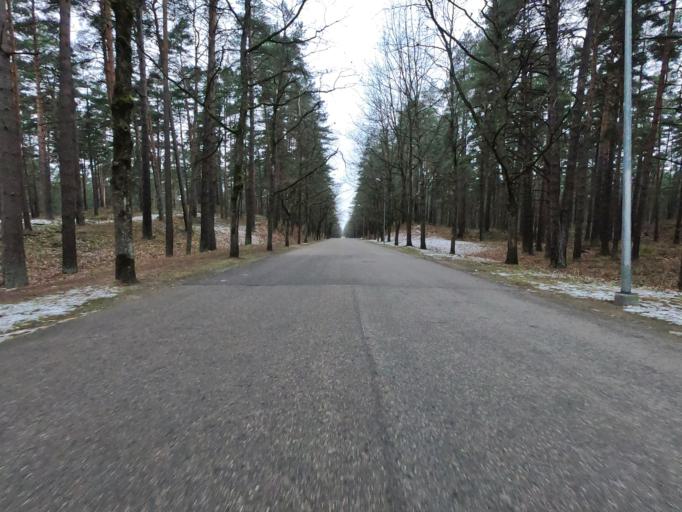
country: LV
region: Riga
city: Jaunciems
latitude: 57.0148
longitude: 24.1487
